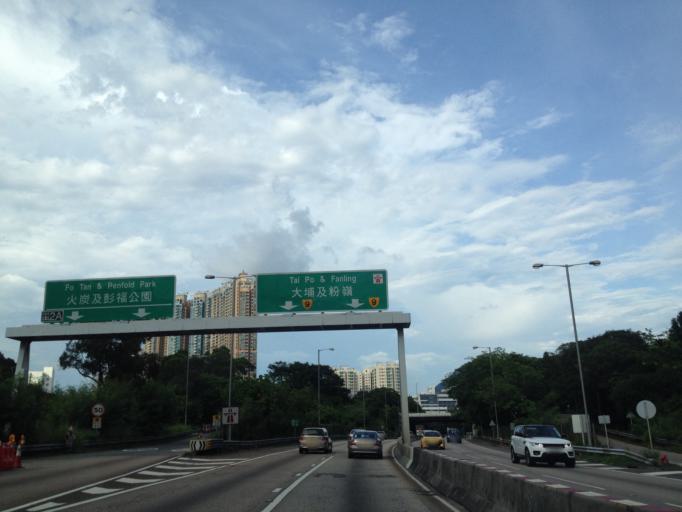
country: HK
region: Sha Tin
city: Sha Tin
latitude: 22.3902
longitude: 114.1947
